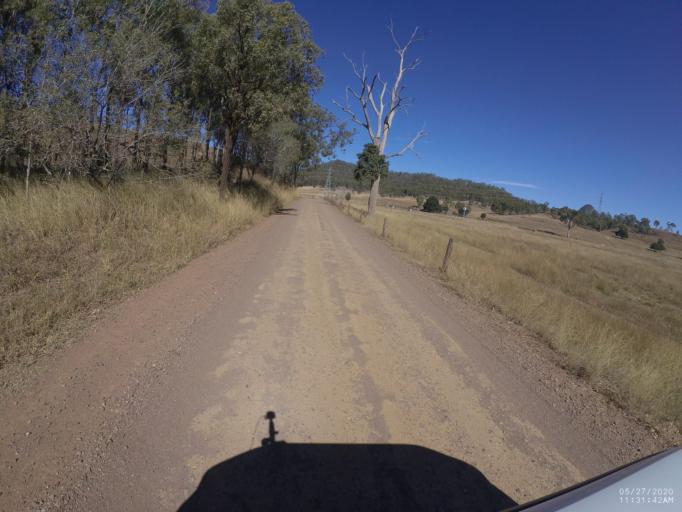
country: AU
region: Queensland
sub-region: Ipswich
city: Redbank Plains
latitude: -27.7442
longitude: 152.8304
